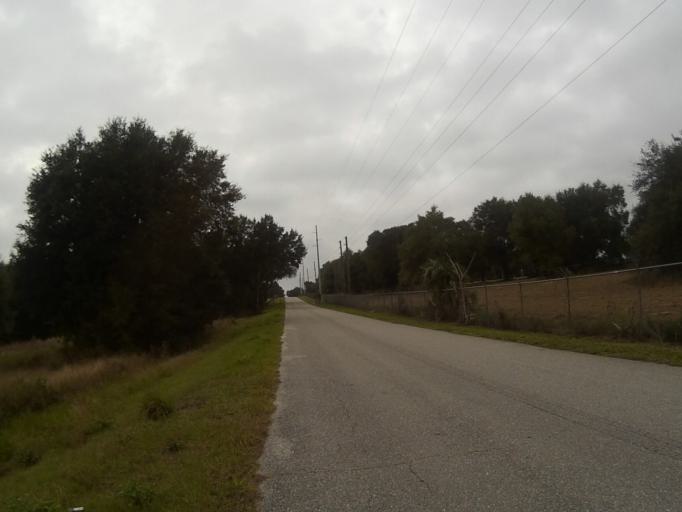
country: US
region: Florida
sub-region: Lake County
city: Umatilla
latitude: 28.9603
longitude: -81.6547
